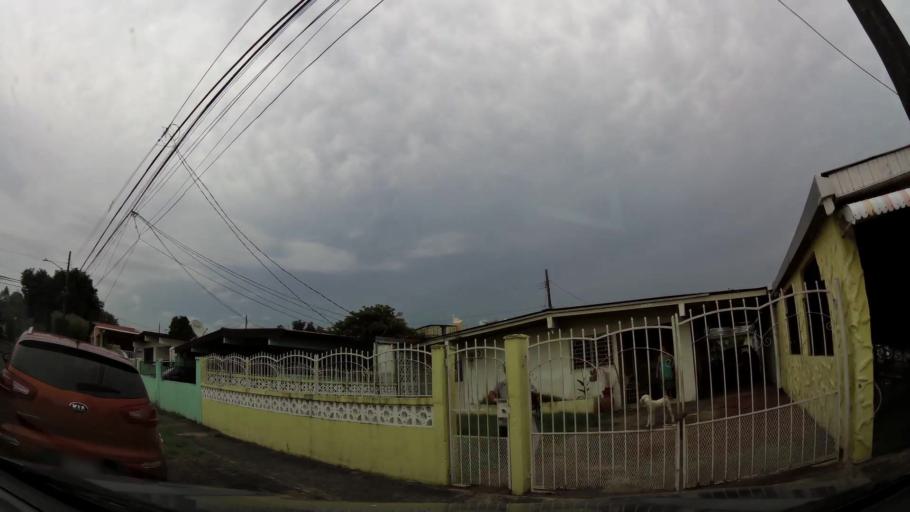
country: PA
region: Panama
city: Panama
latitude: 9.0196
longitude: -79.5240
